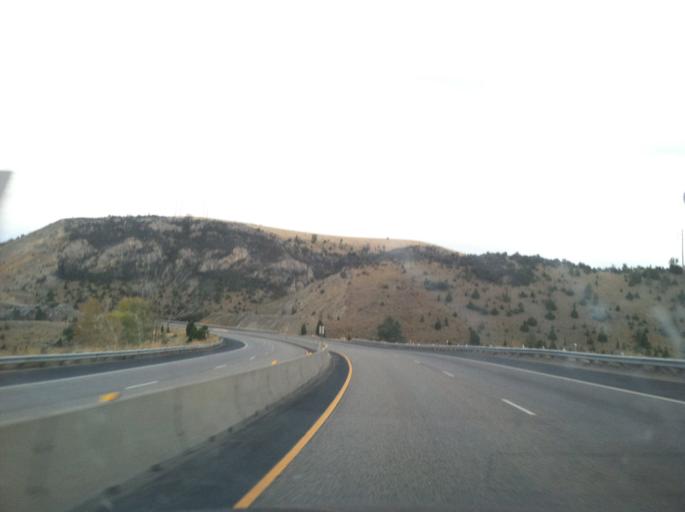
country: US
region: Montana
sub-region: Jefferson County
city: Whitehall
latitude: 45.8758
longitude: -111.8951
